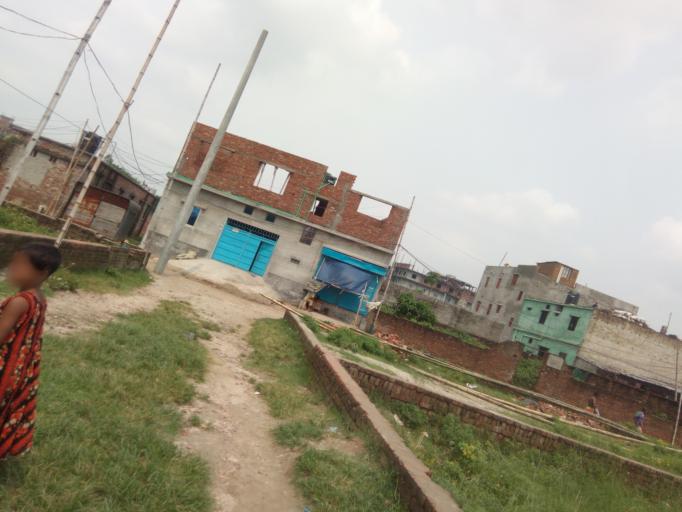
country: BD
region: Dhaka
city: Azimpur
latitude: 23.7419
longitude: 90.3544
